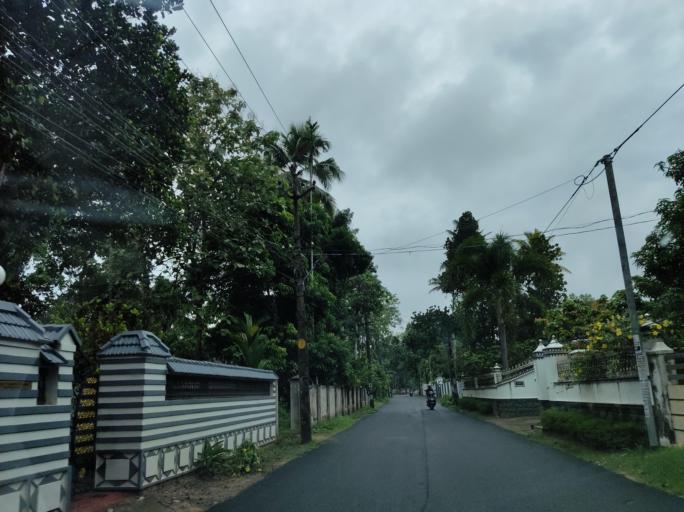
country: IN
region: Kerala
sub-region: Alappuzha
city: Mavelikara
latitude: 9.2486
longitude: 76.5290
